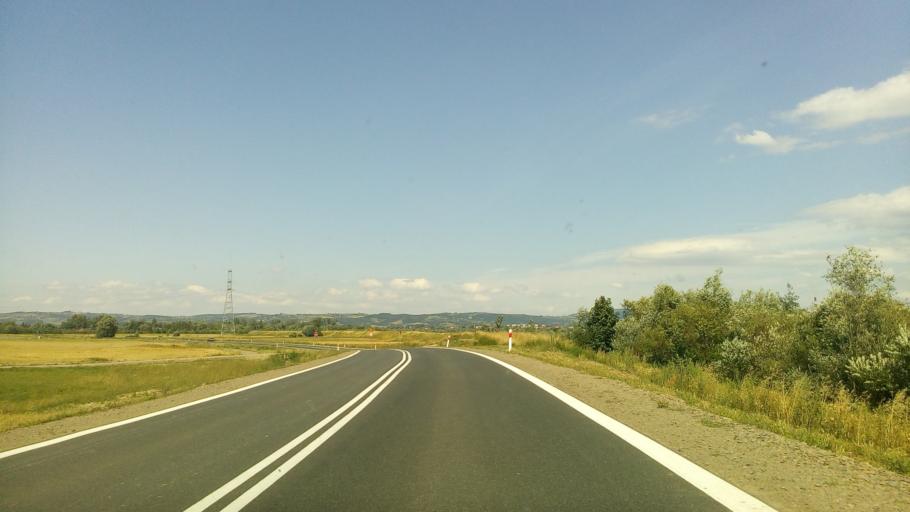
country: PL
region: Lesser Poland Voivodeship
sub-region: Powiat nowosadecki
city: Stary Sacz
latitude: 49.5925
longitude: 20.6447
